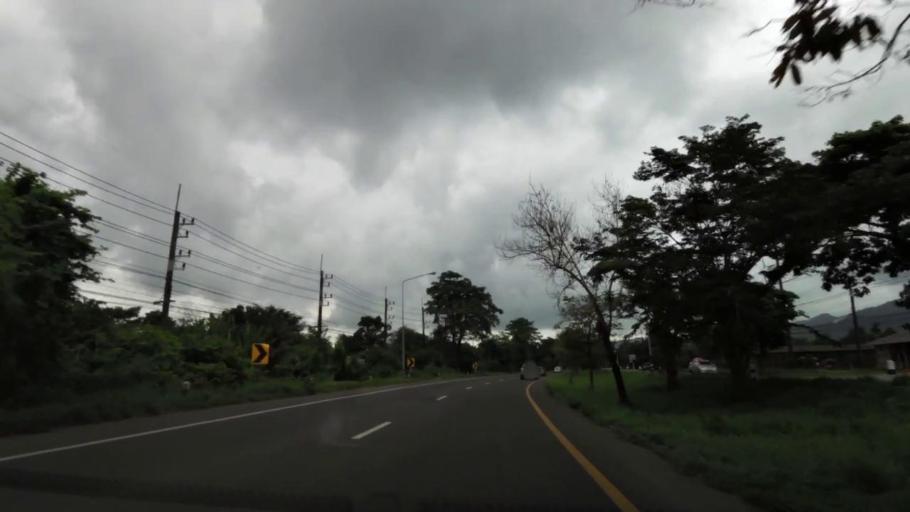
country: TH
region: Chanthaburi
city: Tha Mai
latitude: 12.6768
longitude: 102.0050
